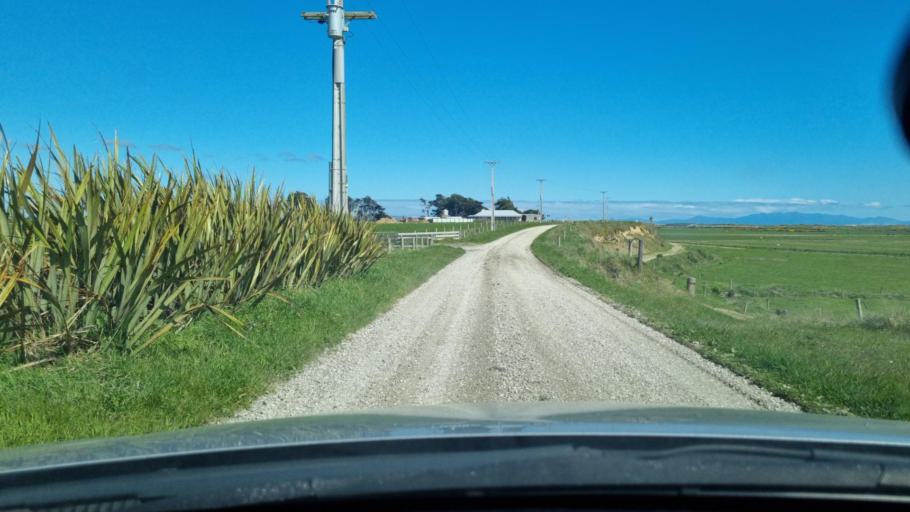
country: NZ
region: Southland
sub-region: Invercargill City
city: Invercargill
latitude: -46.3972
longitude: 168.2576
